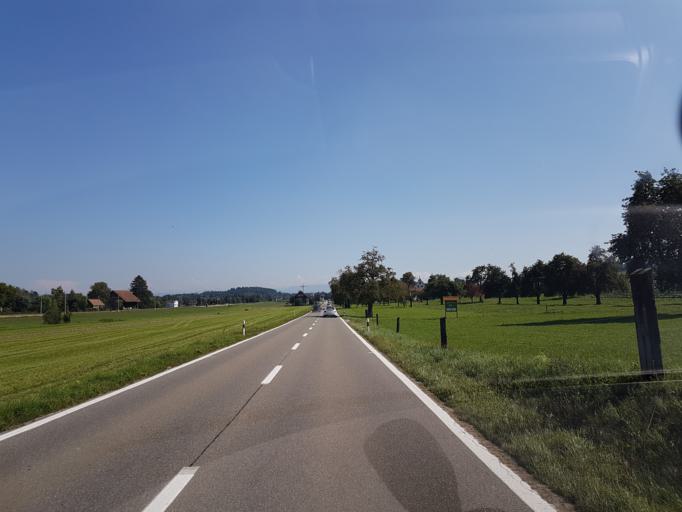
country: CH
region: Aargau
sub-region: Bezirk Muri
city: Muri
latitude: 47.2865
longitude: 8.3269
